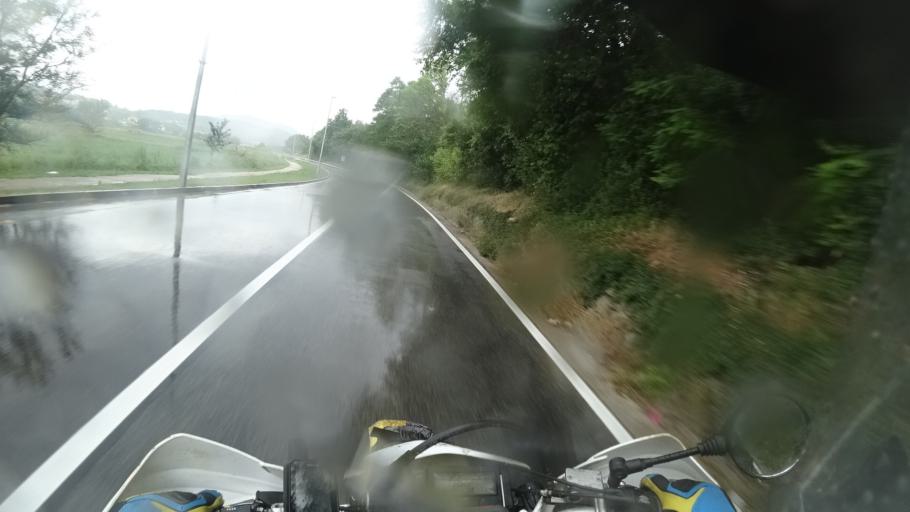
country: HR
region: Sibensko-Kniniska
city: Knin
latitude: 44.0439
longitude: 16.2101
